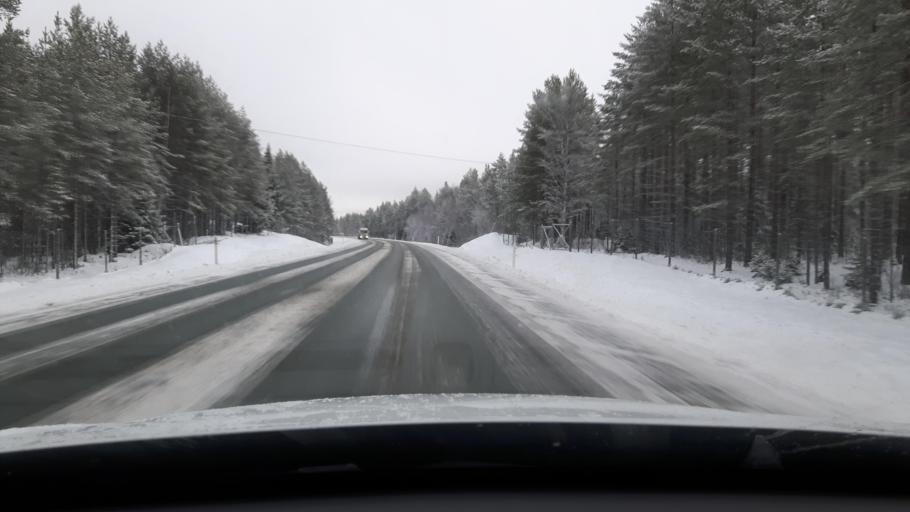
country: SE
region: Vaesterbotten
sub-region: Robertsfors Kommun
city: Robertsfors
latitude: 64.0392
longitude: 20.8454
